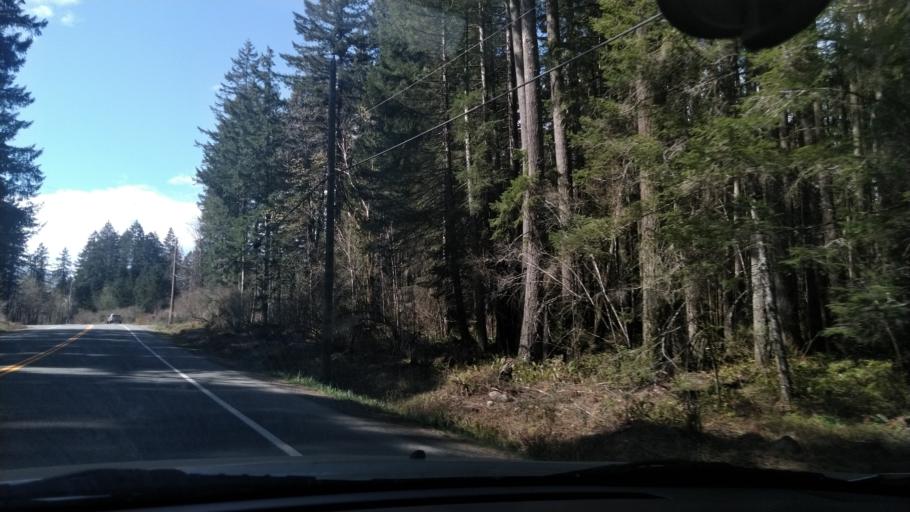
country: CA
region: British Columbia
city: Courtenay
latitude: 49.6958
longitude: -125.0596
